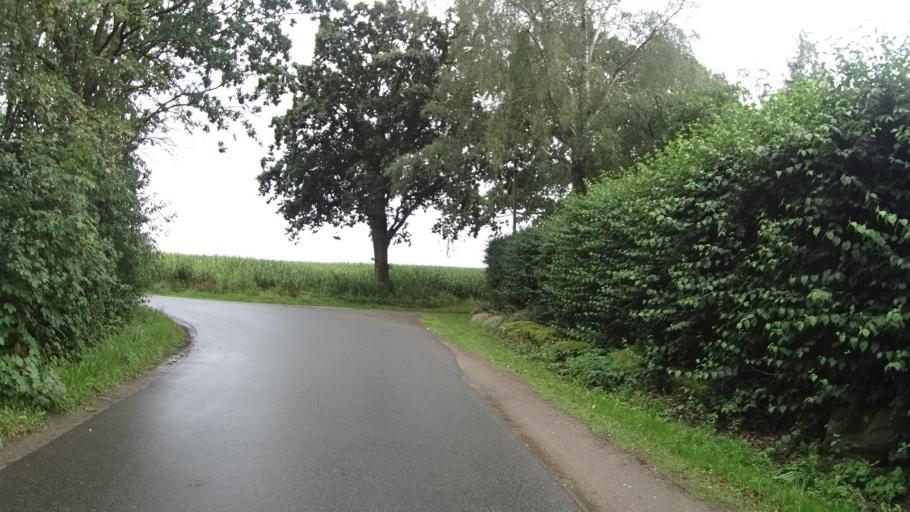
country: DE
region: Schleswig-Holstein
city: Lasbek
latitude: 53.7253
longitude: 10.3877
